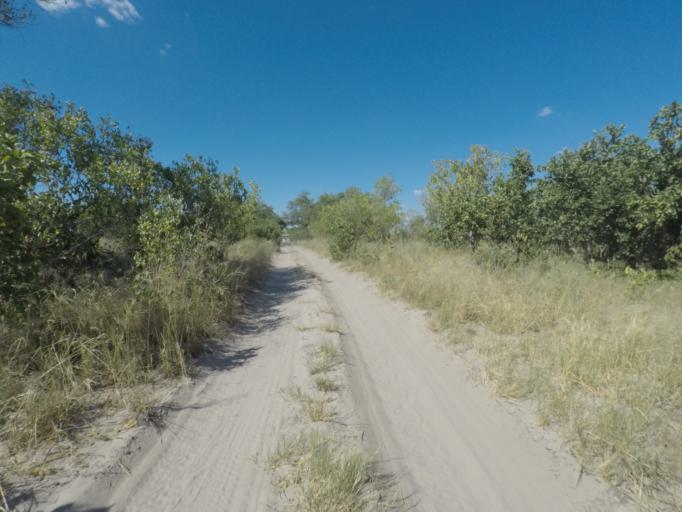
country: BW
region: North West
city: Maun
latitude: -19.4264
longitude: 23.6330
